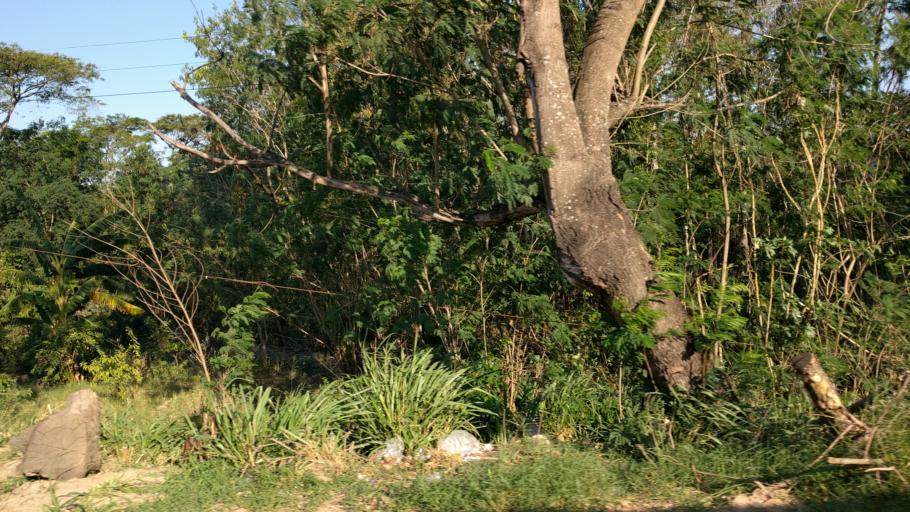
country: BO
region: Santa Cruz
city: Jorochito
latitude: -18.1432
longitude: -63.4810
